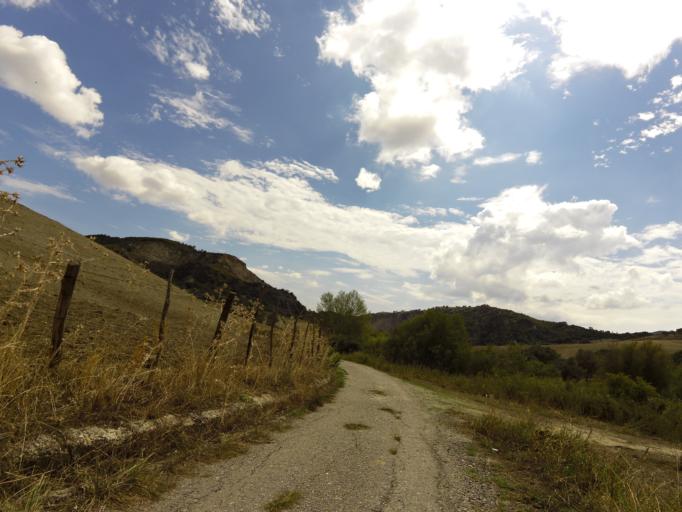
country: IT
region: Calabria
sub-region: Provincia di Reggio Calabria
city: Stilo
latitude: 38.4555
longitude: 16.4654
